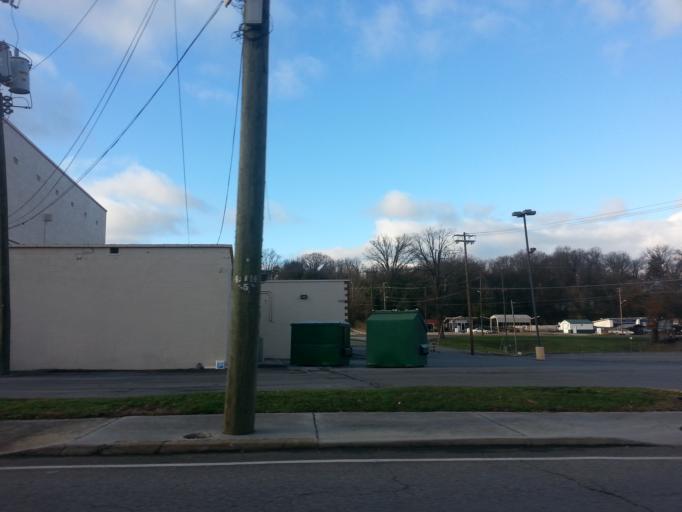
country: US
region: Tennessee
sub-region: Knox County
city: Knoxville
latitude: 36.0030
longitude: -83.8672
